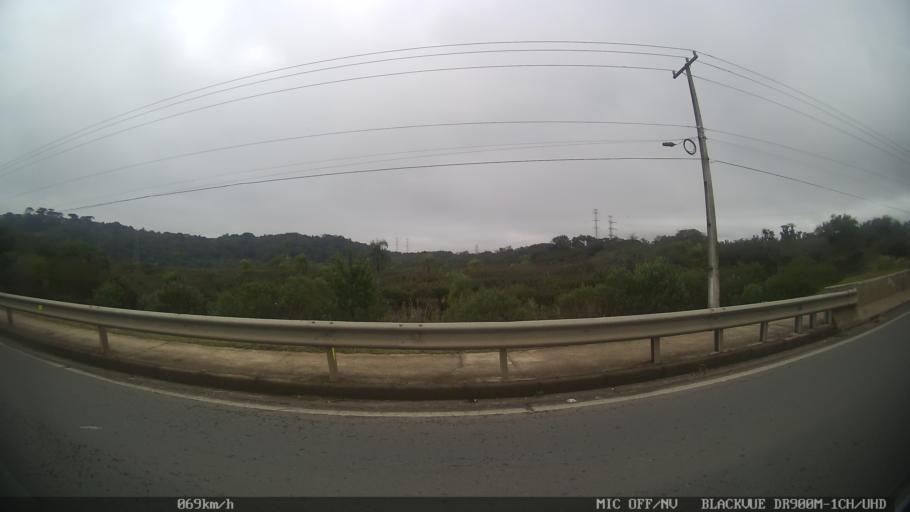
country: BR
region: Parana
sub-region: Sao Jose Dos Pinhais
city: Sao Jose dos Pinhais
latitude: -25.5970
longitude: -49.1737
